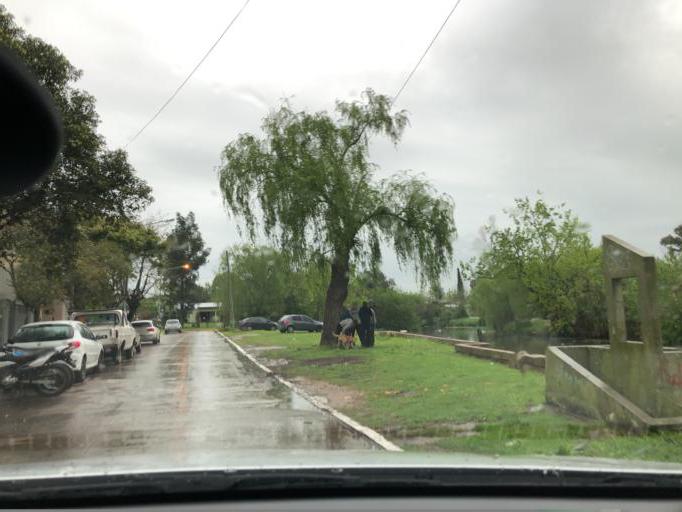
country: AR
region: Buenos Aires
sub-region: Partido de Ensenada
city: Ensenada
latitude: -34.8488
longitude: -57.9209
